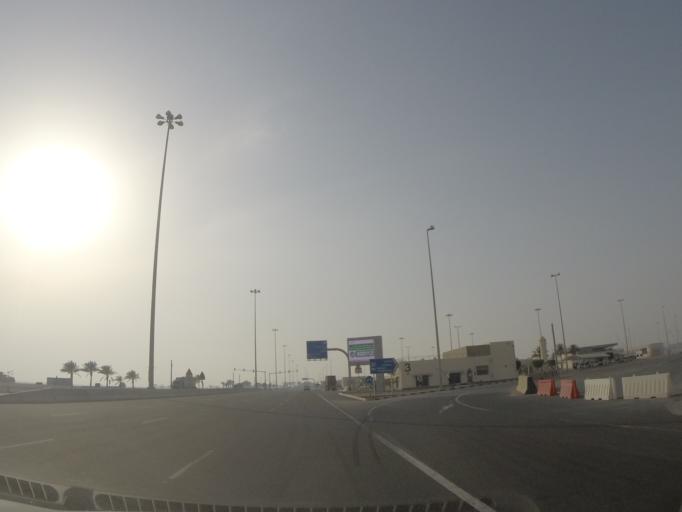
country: AE
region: Abu Dhabi
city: Abu Dhabi
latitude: 24.7767
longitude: 54.7107
